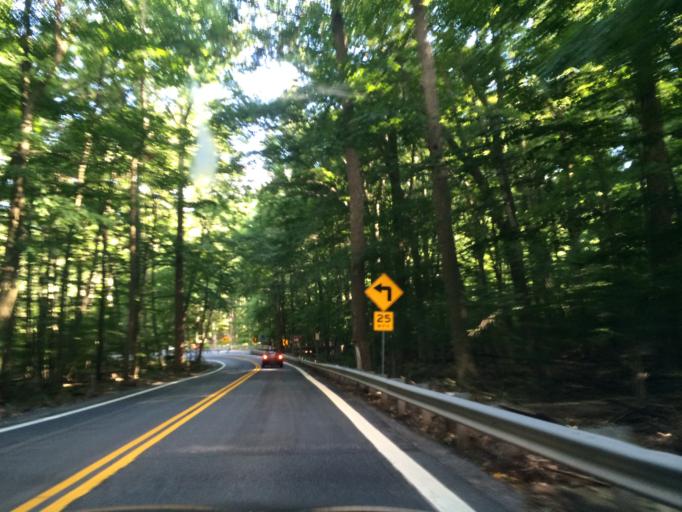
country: US
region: Maryland
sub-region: Frederick County
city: Thurmont
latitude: 39.6334
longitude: -77.4685
